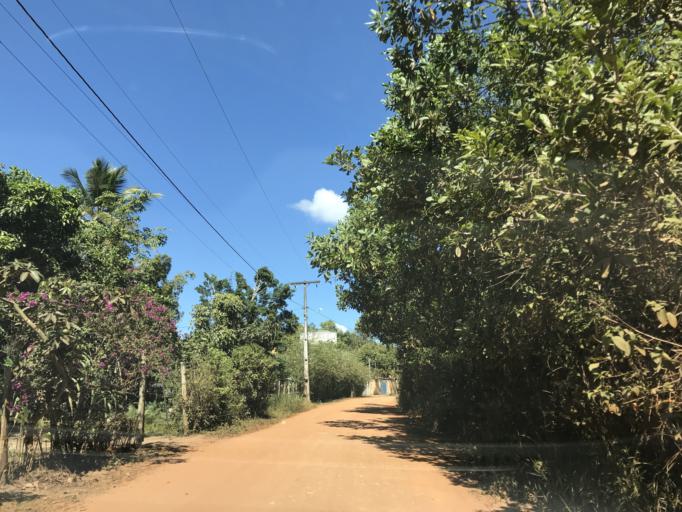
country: BR
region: Bahia
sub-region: Valenca
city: Valenca
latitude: -13.3193
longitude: -39.2402
